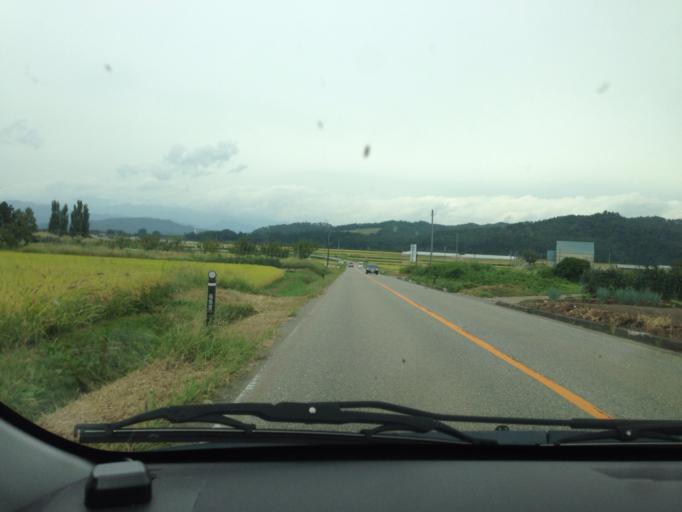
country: JP
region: Fukushima
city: Kitakata
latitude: 37.6010
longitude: 139.8118
